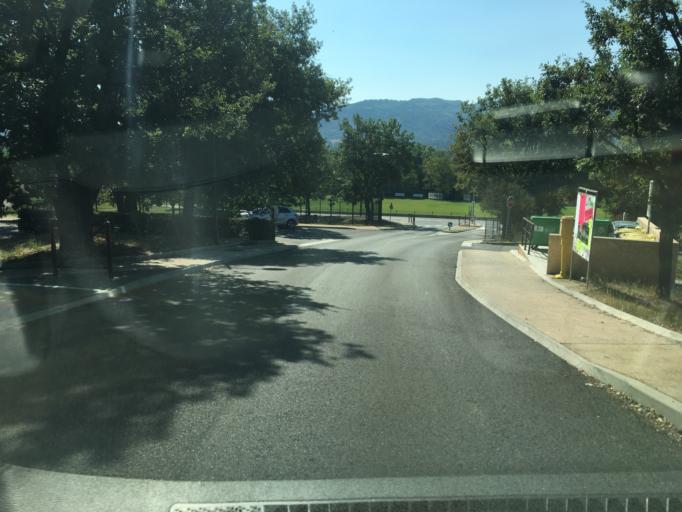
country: FR
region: Provence-Alpes-Cote d'Azur
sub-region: Departement des Alpes-de-Haute-Provence
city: Mallemoisson
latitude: 44.0509
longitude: 6.1418
